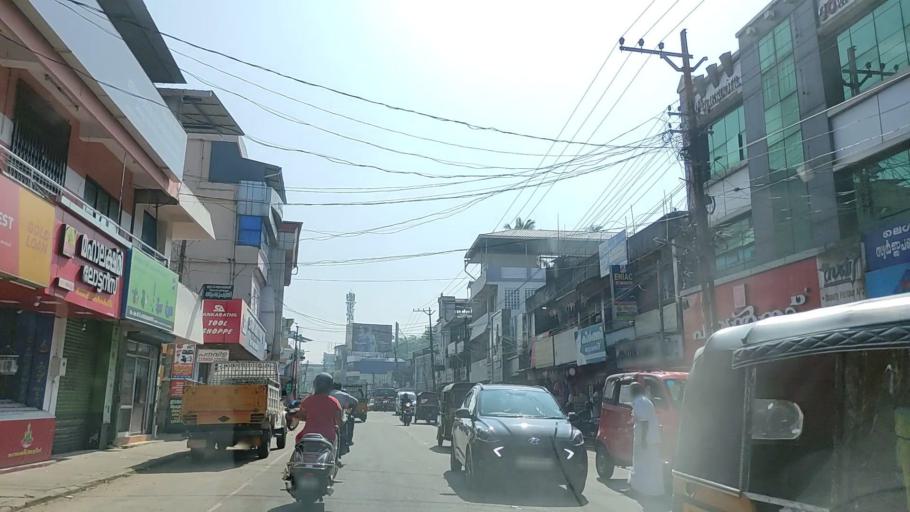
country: IN
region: Kerala
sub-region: Kollam
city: Punalur
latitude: 8.9278
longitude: 76.9129
